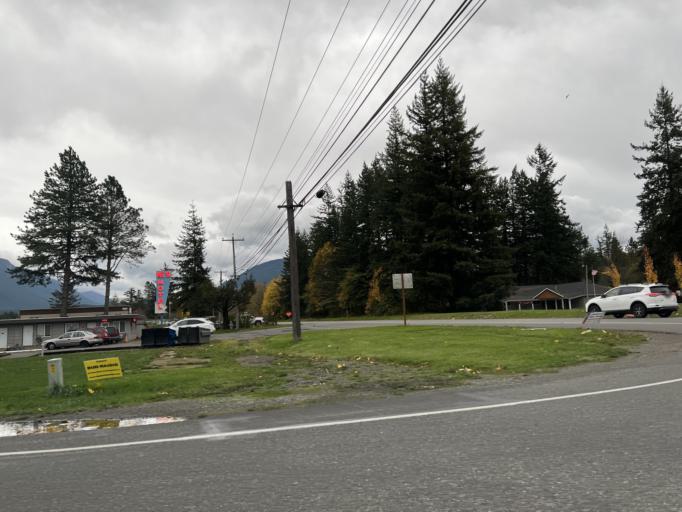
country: US
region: Washington
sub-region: King County
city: Tanner
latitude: 47.4841
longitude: -121.7635
